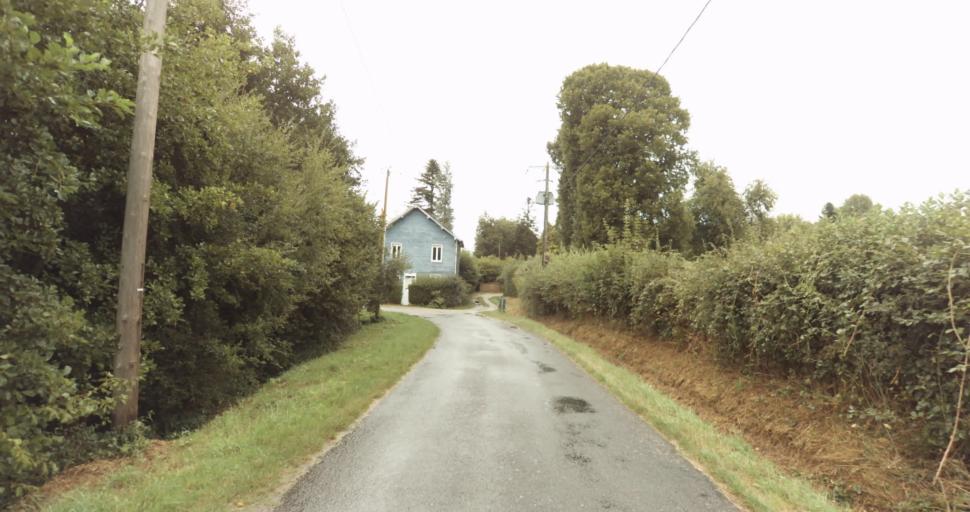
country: FR
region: Lower Normandy
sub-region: Departement de l'Orne
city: Sainte-Gauburge-Sainte-Colombe
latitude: 48.7104
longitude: 0.4315
